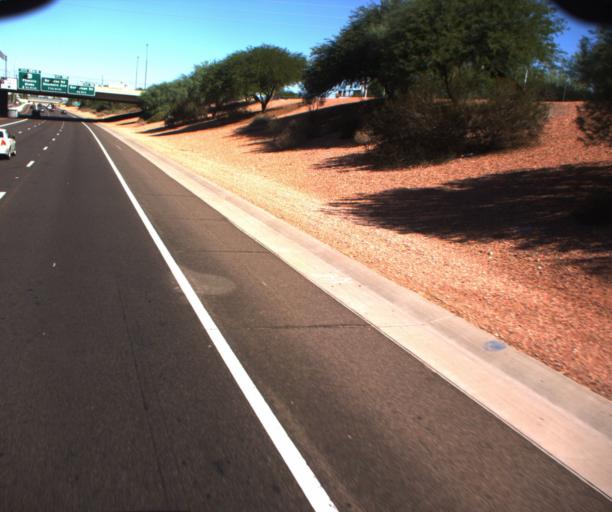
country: US
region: Arizona
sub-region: Maricopa County
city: San Carlos
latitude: 33.3479
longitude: -111.8935
